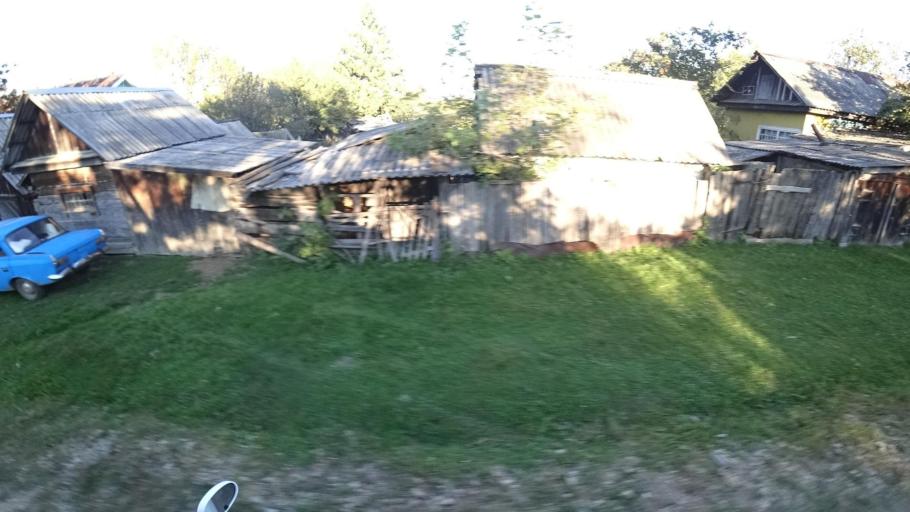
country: RU
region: Primorskiy
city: Kirovskiy
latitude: 44.8331
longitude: 133.5729
